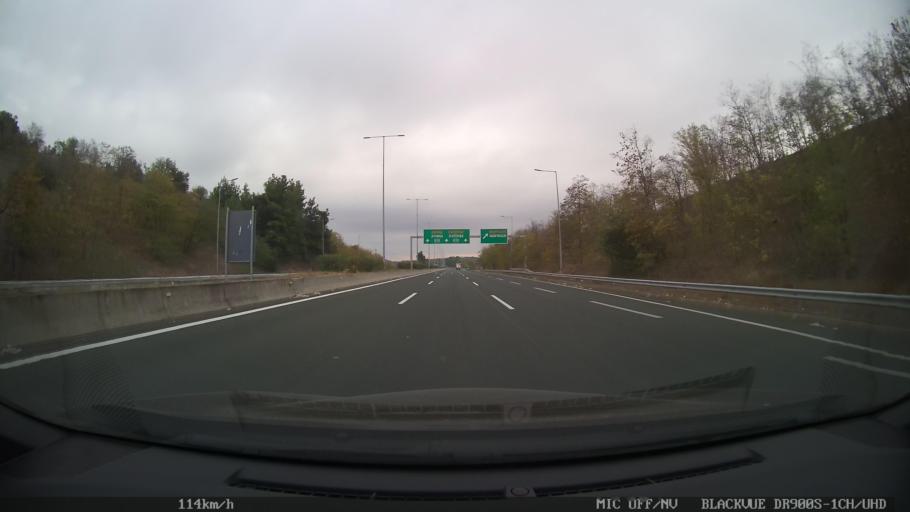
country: GR
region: Central Macedonia
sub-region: Nomos Pierias
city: Makrygialos
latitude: 40.4229
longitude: 22.5898
